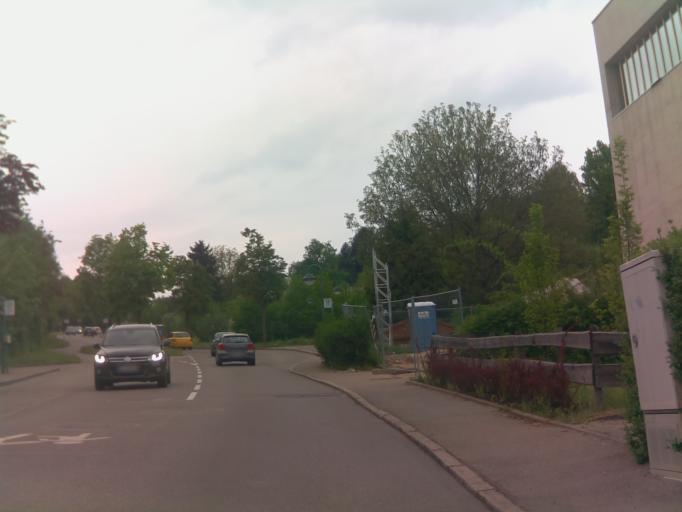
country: DE
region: Baden-Wuerttemberg
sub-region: Tuebingen Region
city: Pliezhausen
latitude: 48.5628
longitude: 9.2059
